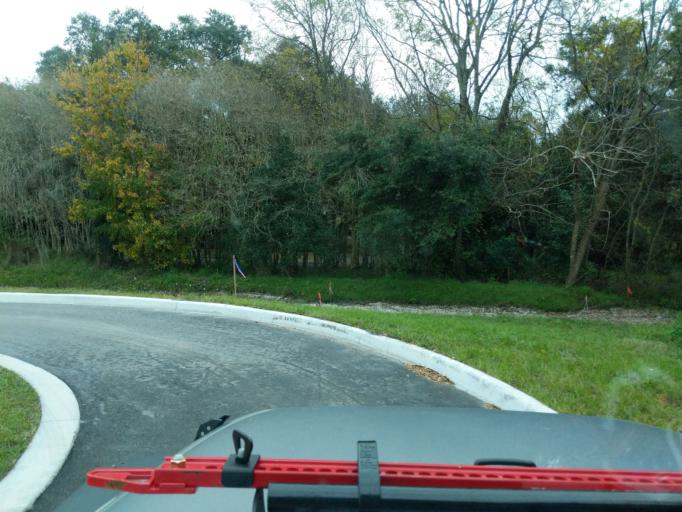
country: US
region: Florida
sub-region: Orange County
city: Oakland
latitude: 28.5530
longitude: -81.6145
